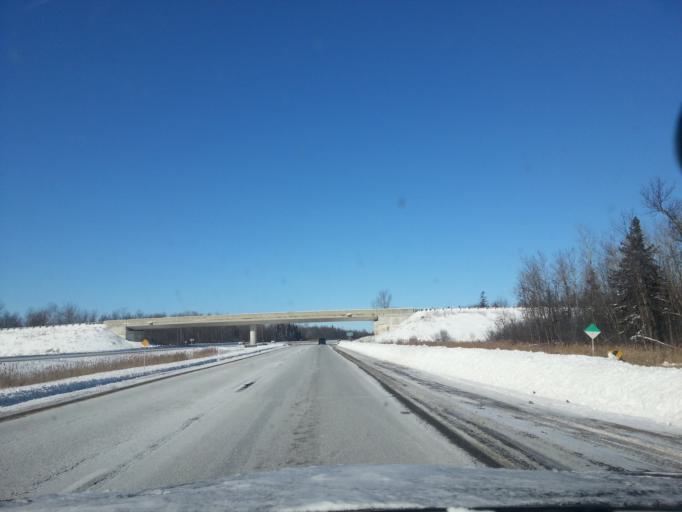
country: CA
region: Ontario
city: Bells Corners
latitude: 45.2965
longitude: -76.0220
